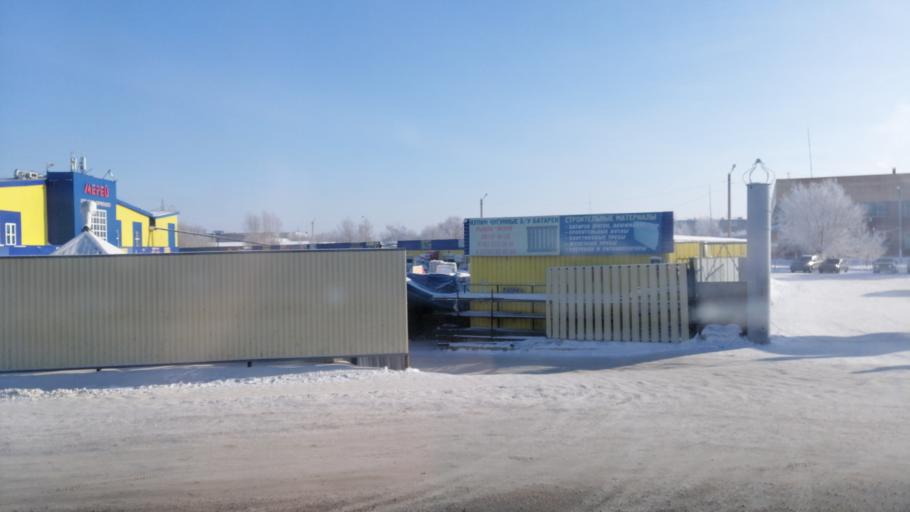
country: KZ
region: Aqtoebe
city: Aqtobe
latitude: 50.2946
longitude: 57.1977
